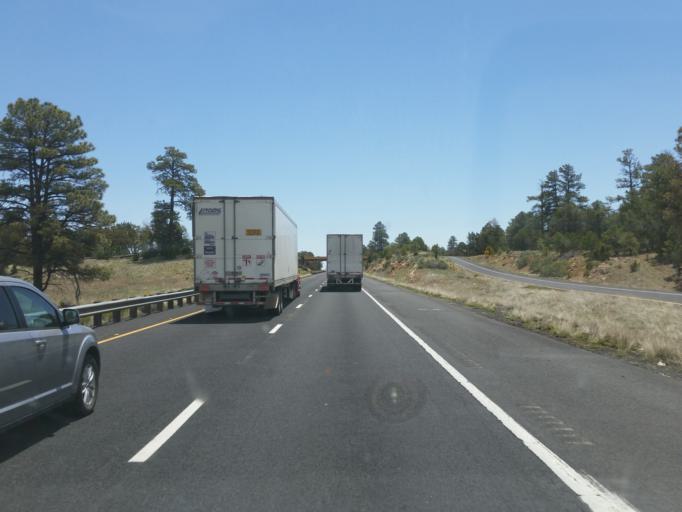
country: US
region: Arizona
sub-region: Coconino County
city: Flagstaff
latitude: 35.2092
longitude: -111.5209
